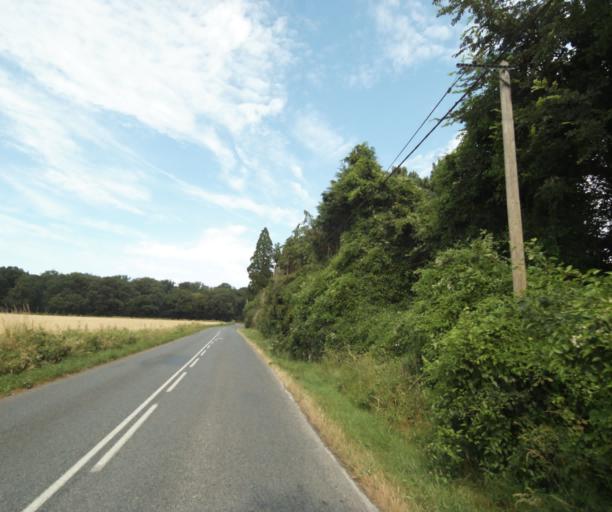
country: FR
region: Ile-de-France
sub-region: Departement de Seine-et-Marne
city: Chailly-en-Biere
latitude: 48.4792
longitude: 2.6236
